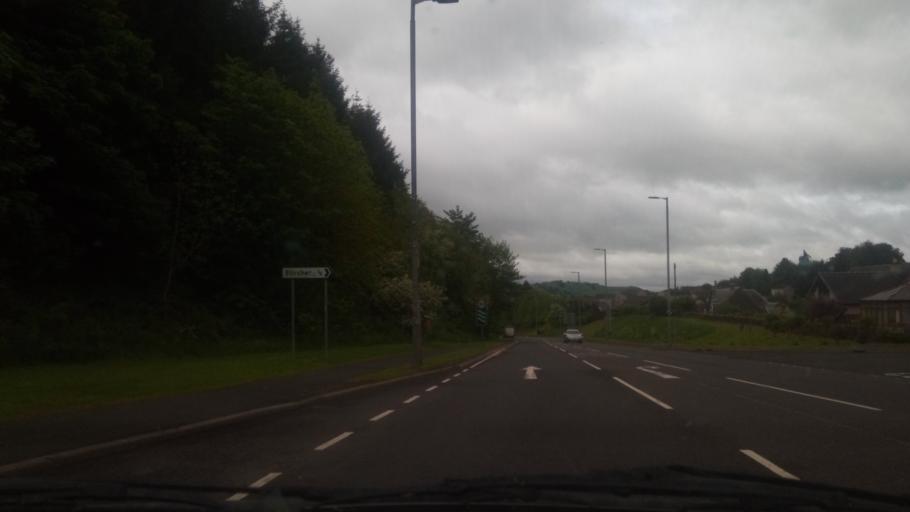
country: GB
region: Scotland
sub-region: The Scottish Borders
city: Hawick
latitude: 55.4377
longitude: -2.7782
